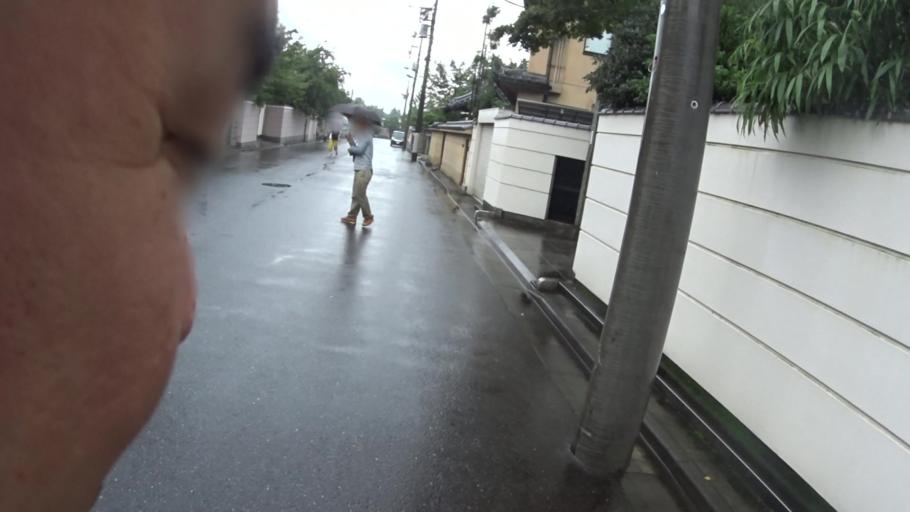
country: JP
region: Saitama
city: Wako
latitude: 35.7418
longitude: 139.6493
